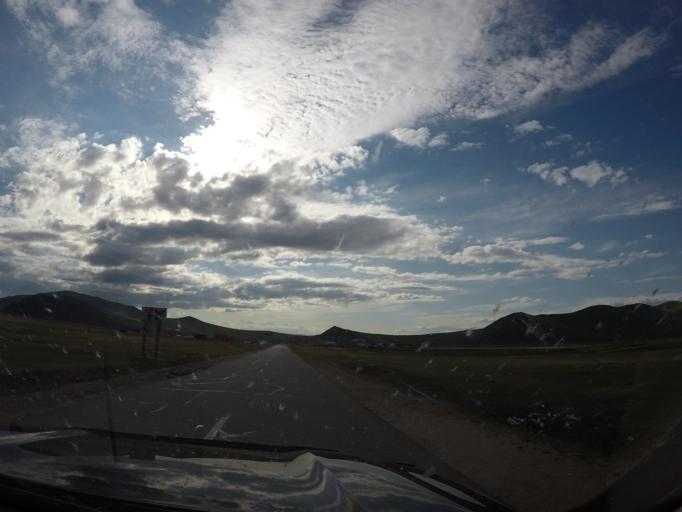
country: MN
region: Central Aimak
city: Bayandelger
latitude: 47.6930
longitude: 108.4812
